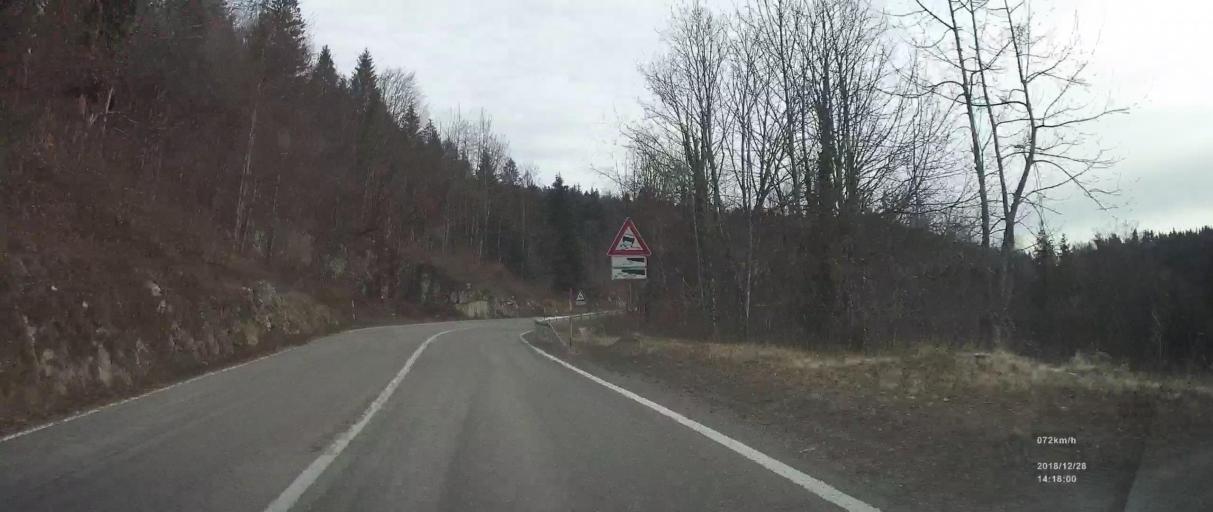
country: HR
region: Primorsko-Goranska
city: Vrbovsko
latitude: 45.4163
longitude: 15.0563
